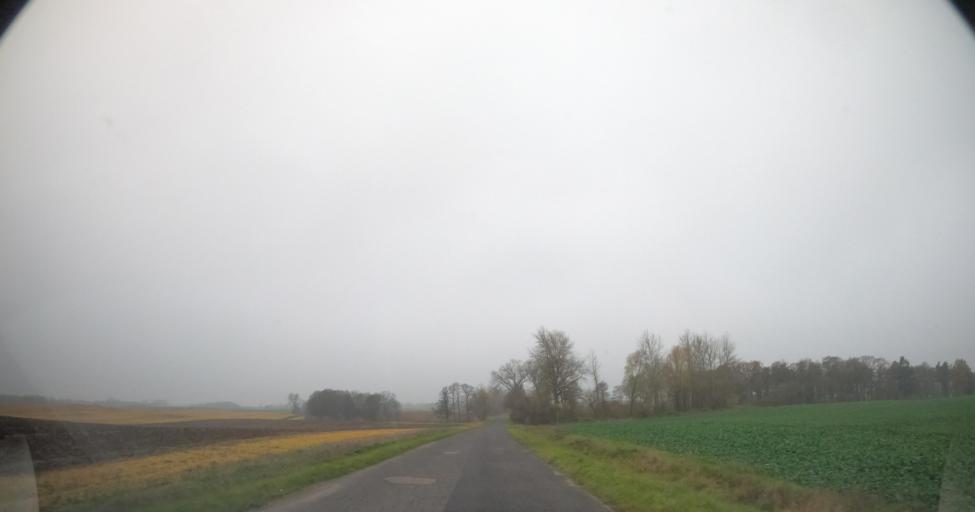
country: PL
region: West Pomeranian Voivodeship
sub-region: Powiat drawski
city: Drawsko Pomorskie
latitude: 53.6030
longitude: 15.7374
